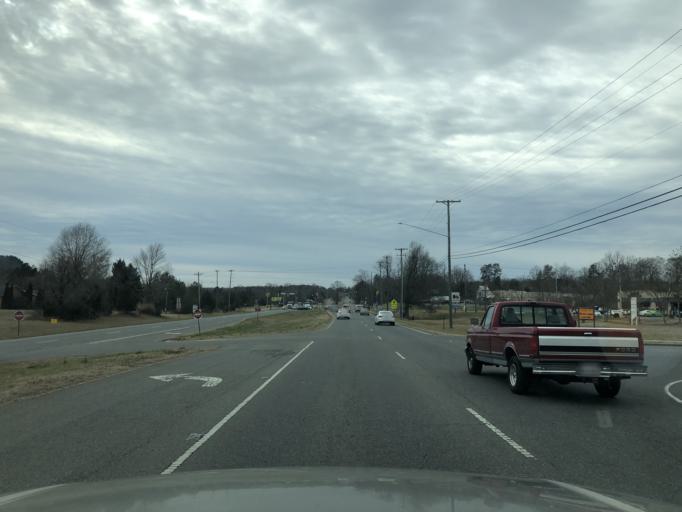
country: US
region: North Carolina
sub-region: Gaston County
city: Bessemer City
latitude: 35.2576
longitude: -81.2540
